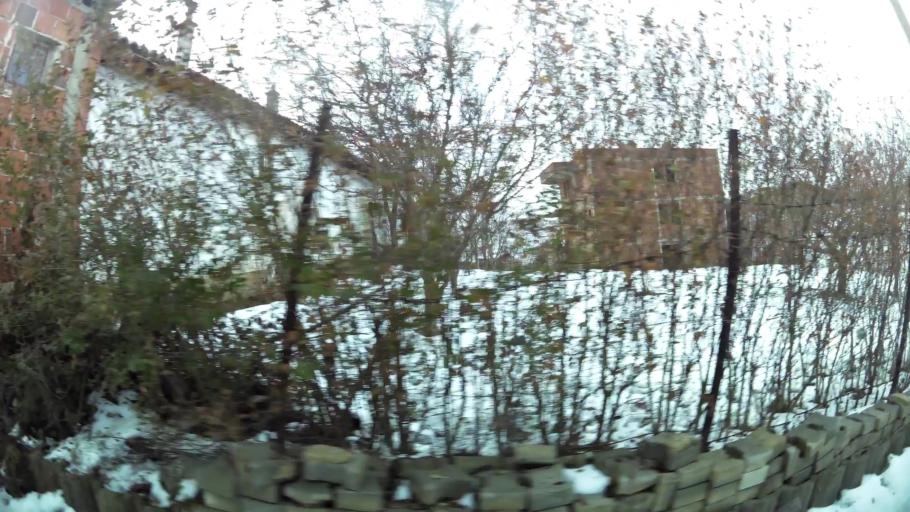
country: XK
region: Pristina
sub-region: Komuna e Prishtines
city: Pristina
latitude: 42.6899
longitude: 21.1732
